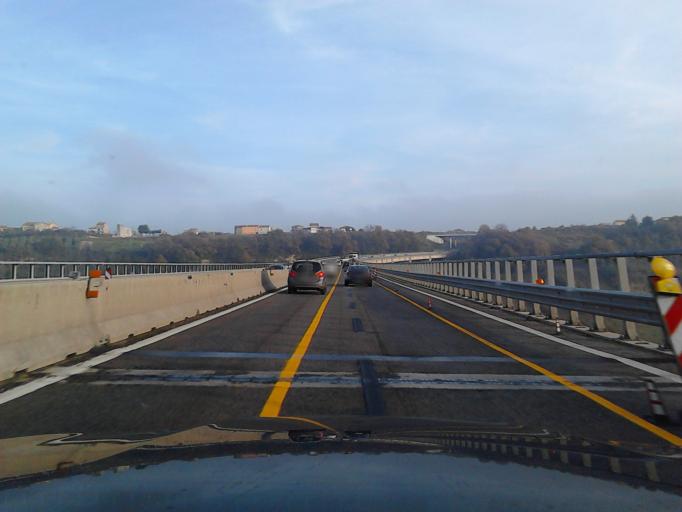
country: IT
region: Abruzzo
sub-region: Provincia di Chieti
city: Marina di San Vito
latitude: 42.3131
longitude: 14.4143
